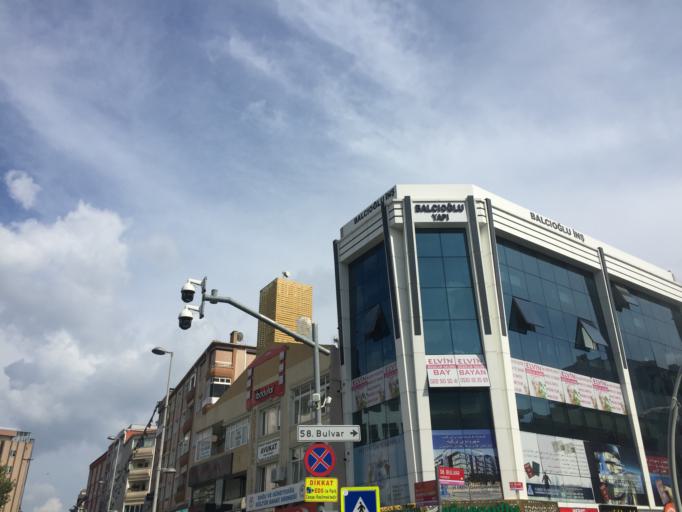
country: TR
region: Istanbul
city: Zeytinburnu
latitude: 40.9945
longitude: 28.9040
